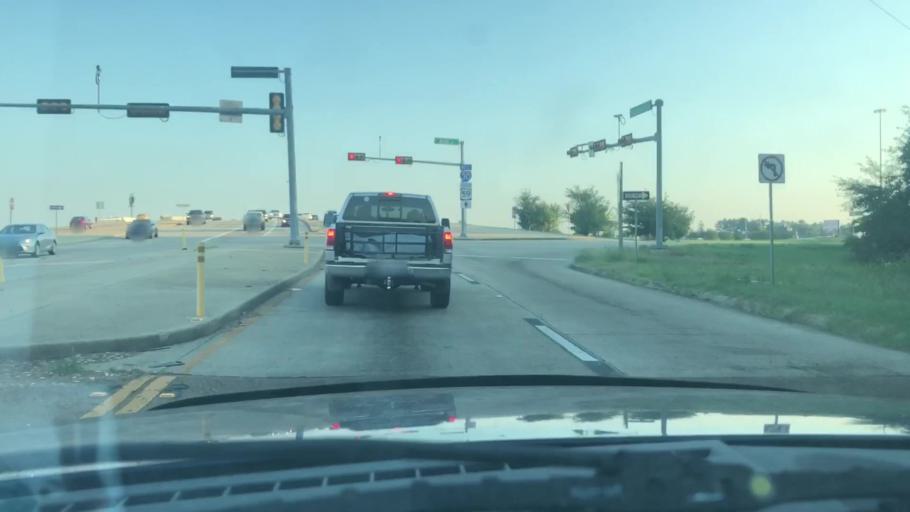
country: US
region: Arkansas
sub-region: Miller County
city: Texarkana
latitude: 33.4635
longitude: -94.0659
